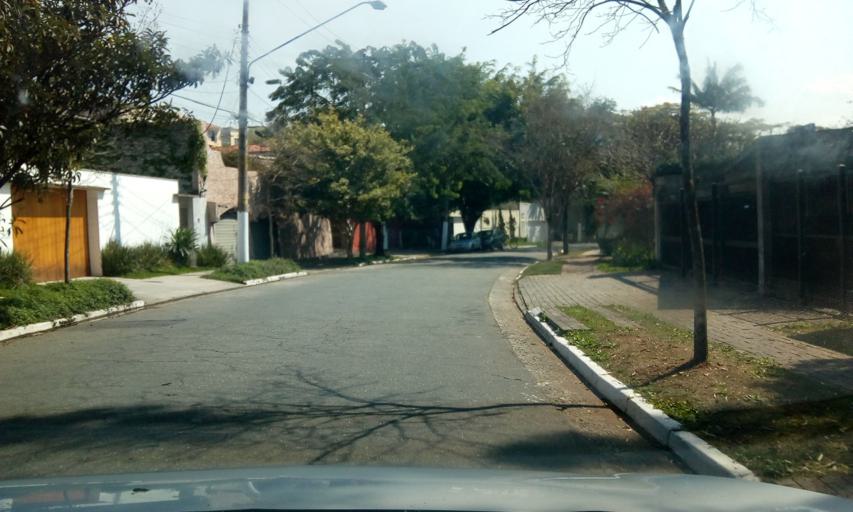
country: BR
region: Sao Paulo
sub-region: Osasco
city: Osasco
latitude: -23.5301
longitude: -46.7167
